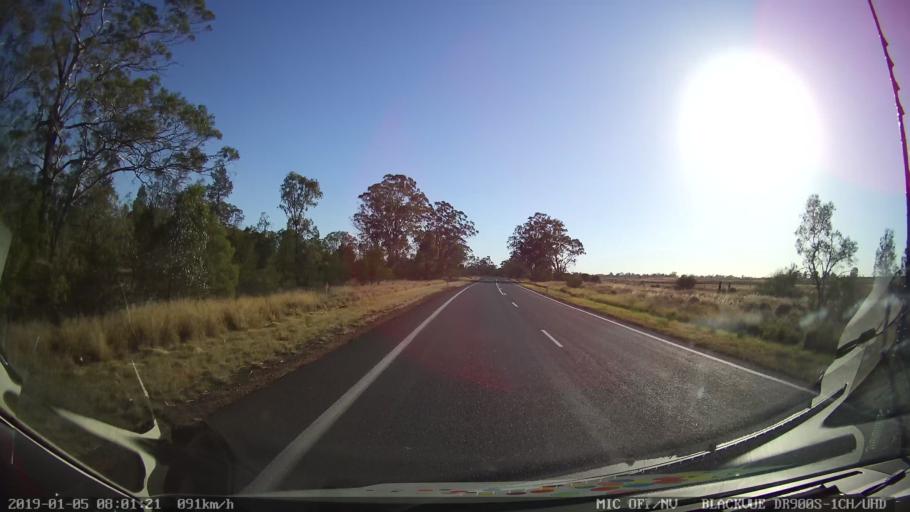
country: AU
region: New South Wales
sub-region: Gilgandra
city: Gilgandra
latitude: -31.6872
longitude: 148.7012
